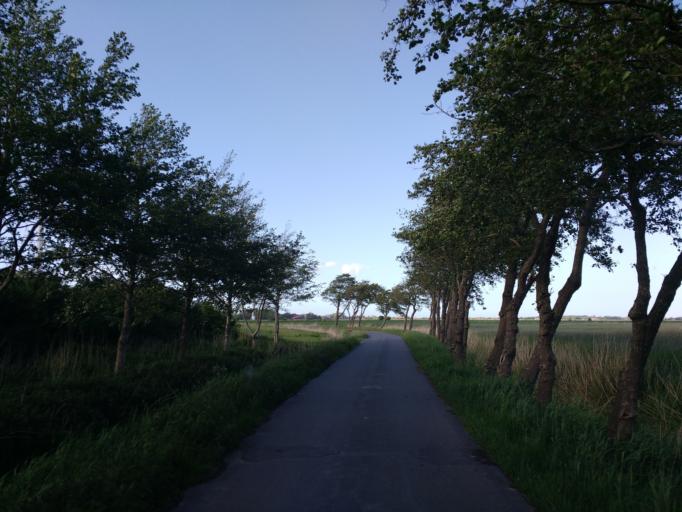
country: DE
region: Lower Saxony
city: Schillig
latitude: 53.6883
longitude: 7.9357
